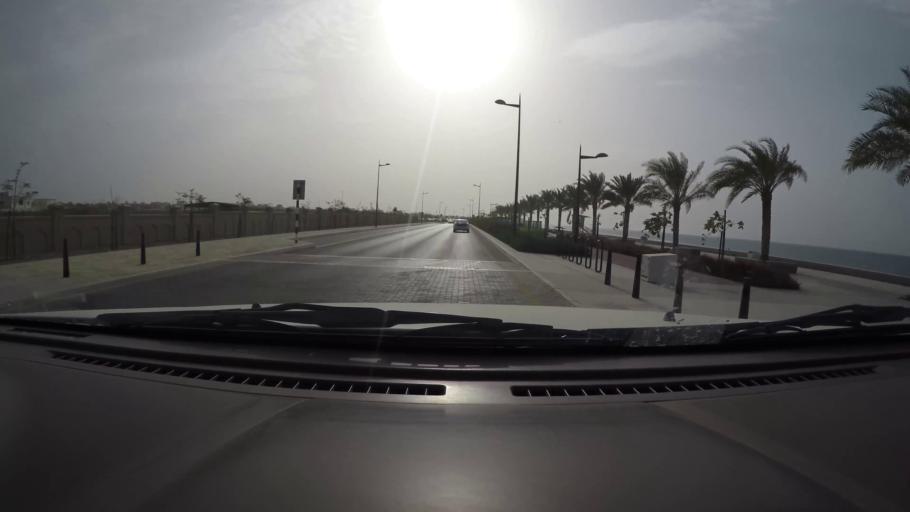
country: OM
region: Muhafazat Masqat
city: As Sib al Jadidah
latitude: 23.6957
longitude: 58.1546
